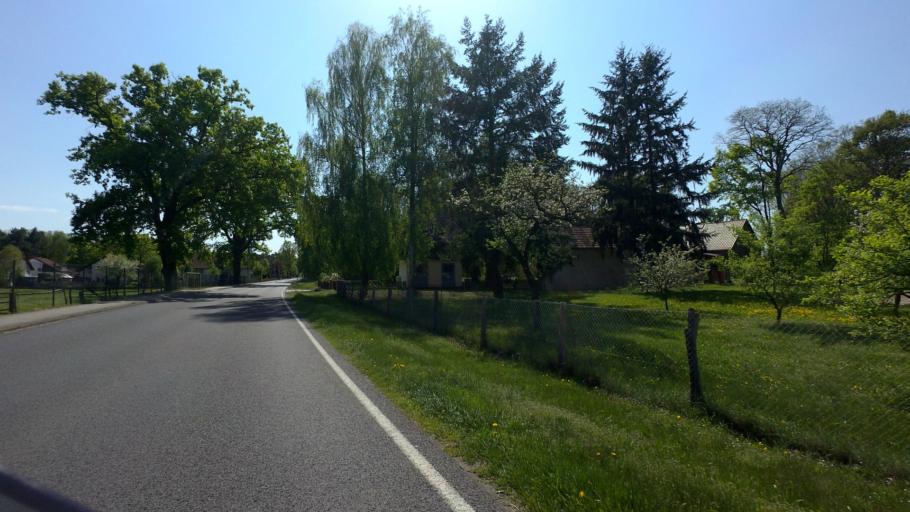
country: DE
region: Brandenburg
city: Tauche
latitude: 52.1164
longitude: 14.1908
